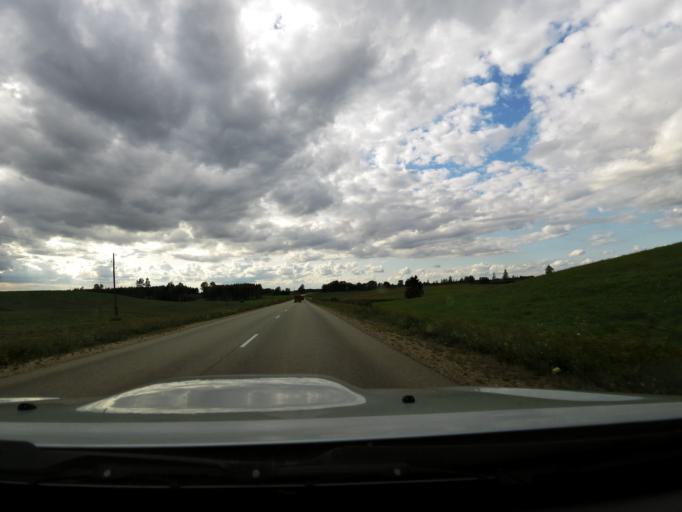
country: LV
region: Ilukste
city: Ilukste
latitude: 55.9824
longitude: 25.9973
